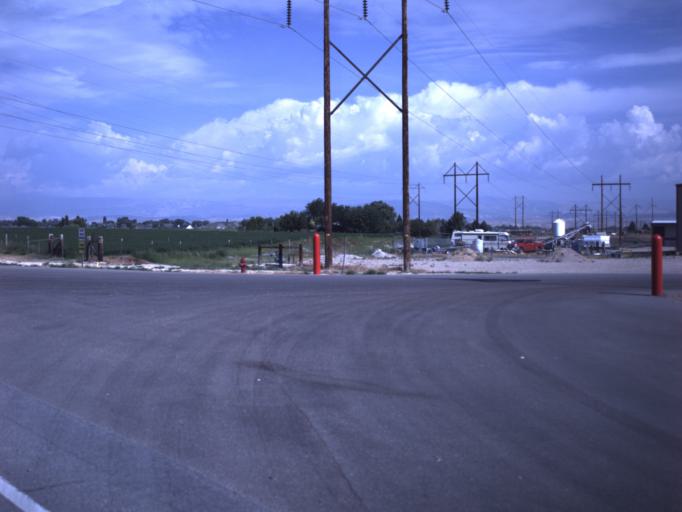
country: US
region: Utah
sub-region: Uintah County
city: Naples
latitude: 40.3994
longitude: -109.4644
